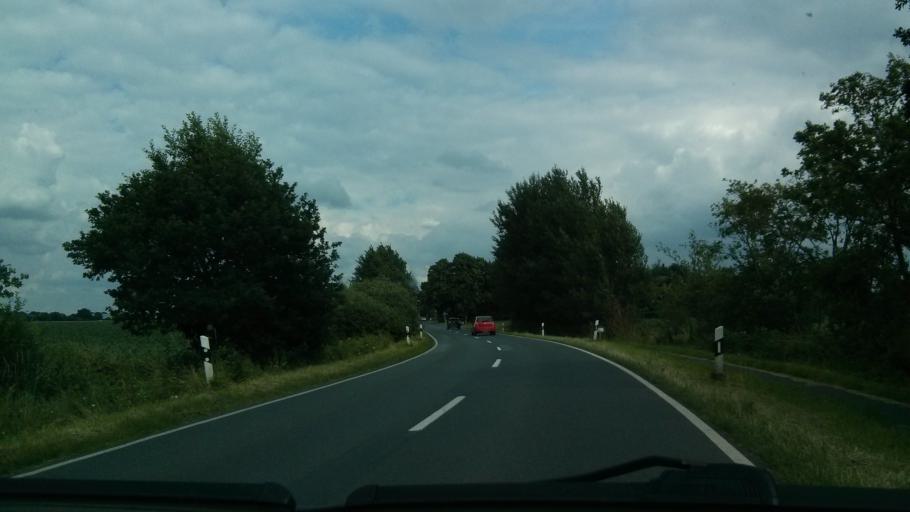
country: DE
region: Lower Saxony
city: Kuhrstedt
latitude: 53.5104
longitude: 8.7696
